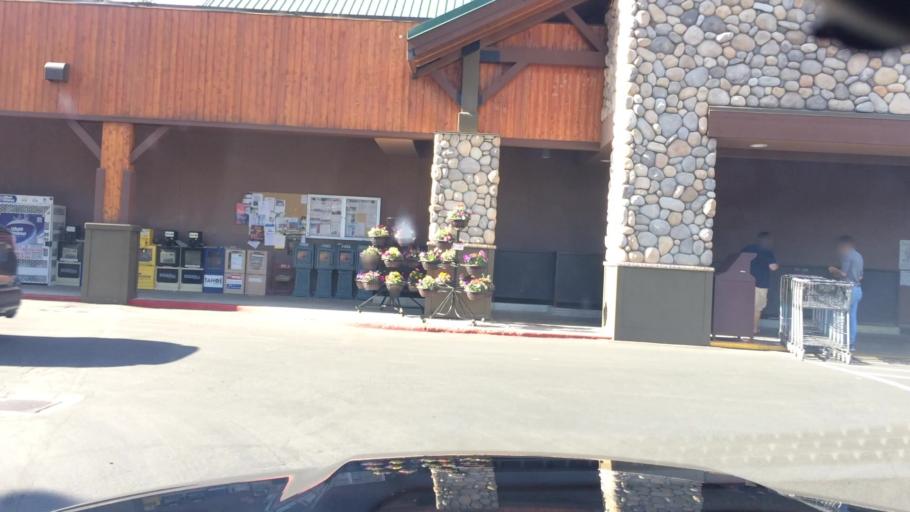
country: US
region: Nevada
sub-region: Washoe County
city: Incline Village
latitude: 39.2505
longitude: -119.9500
